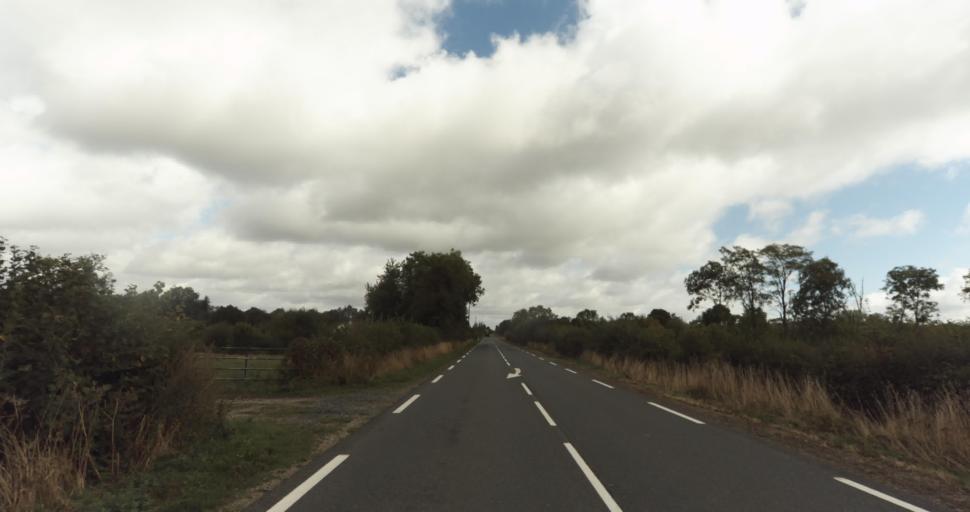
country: FR
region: Lower Normandy
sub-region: Departement de l'Orne
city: Vimoutiers
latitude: 48.8703
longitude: 0.2536
